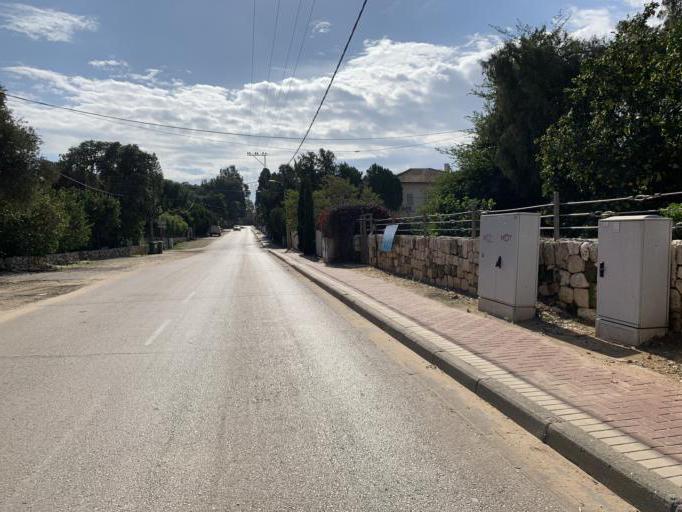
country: IL
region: Central District
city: Ra'anana
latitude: 32.1699
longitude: 34.8754
